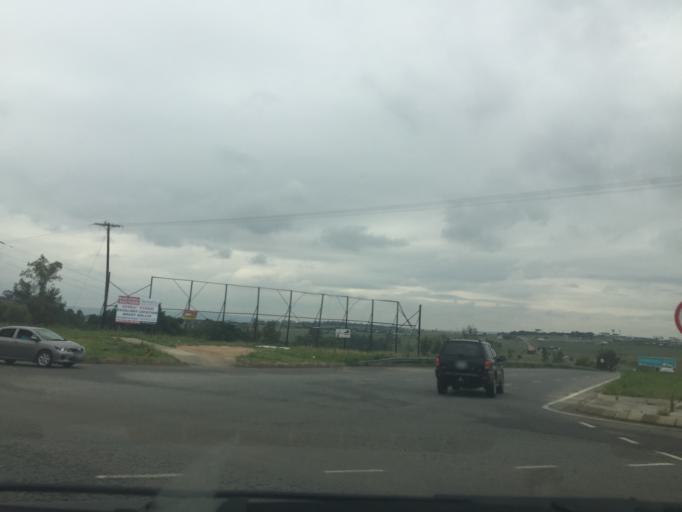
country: ZA
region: Gauteng
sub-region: City of Johannesburg Metropolitan Municipality
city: Diepsloot
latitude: -25.9430
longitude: 27.9090
